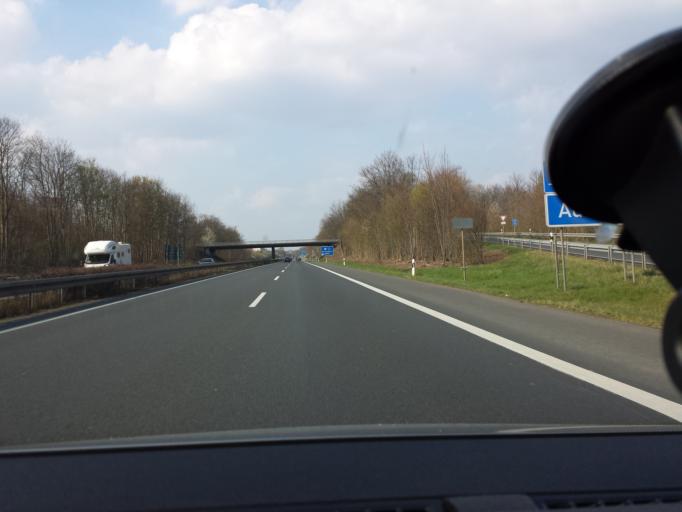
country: DE
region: Lower Saxony
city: Leiferde
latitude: 52.2139
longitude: 10.5345
